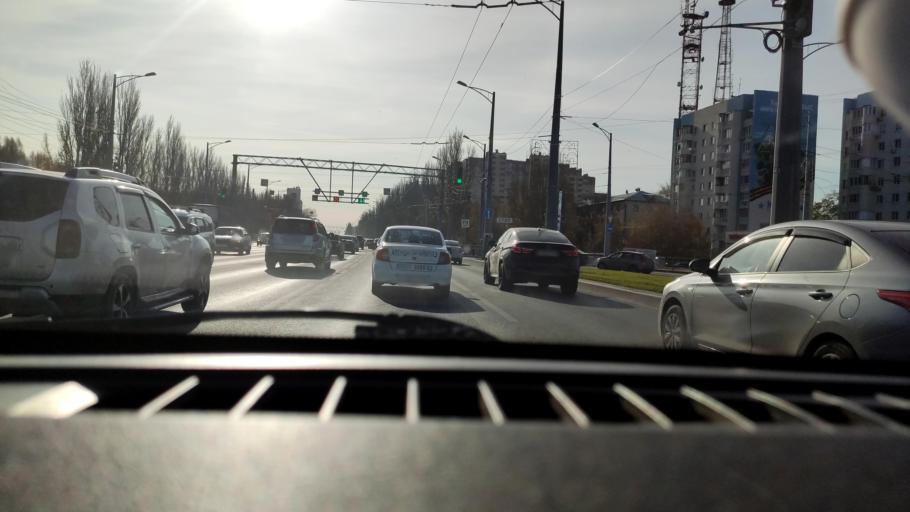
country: RU
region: Samara
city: Samara
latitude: 53.2337
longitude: 50.1977
